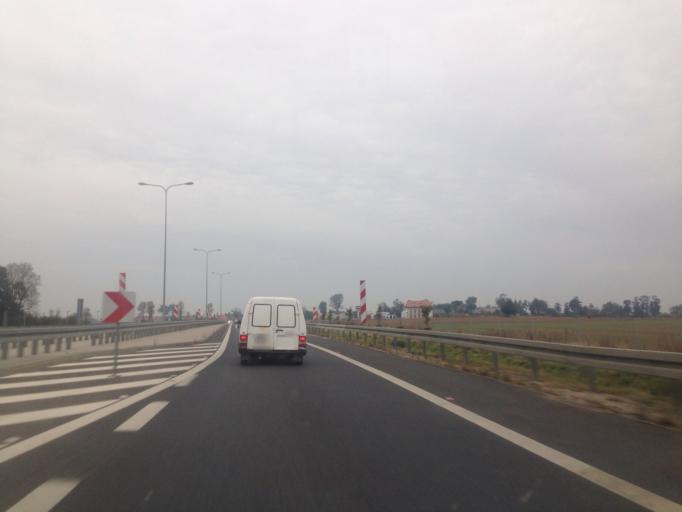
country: PL
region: Greater Poland Voivodeship
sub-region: Powiat gnieznienski
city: Lubowo
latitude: 52.5172
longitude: 17.4885
